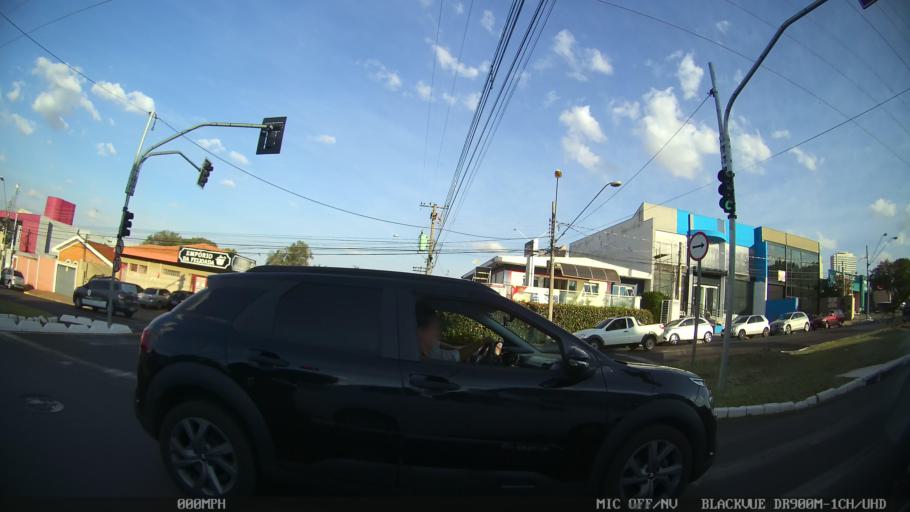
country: BR
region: Sao Paulo
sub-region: Ribeirao Preto
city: Ribeirao Preto
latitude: -21.1946
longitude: -47.8034
